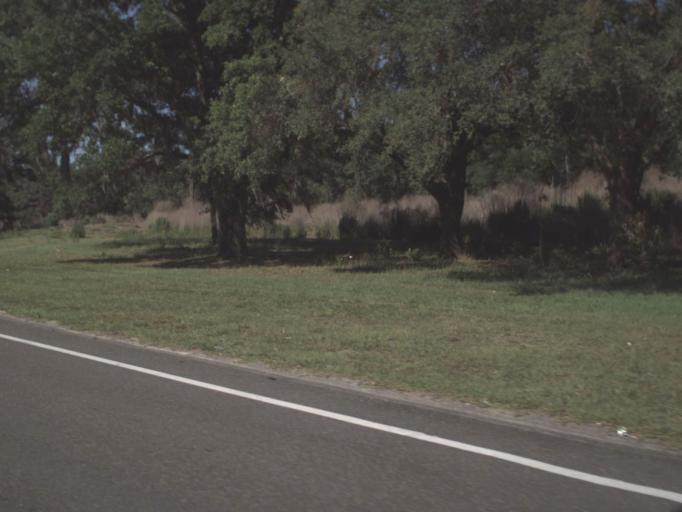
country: US
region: Florida
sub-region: Marion County
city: Dunnellon
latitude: 29.0944
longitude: -82.4513
